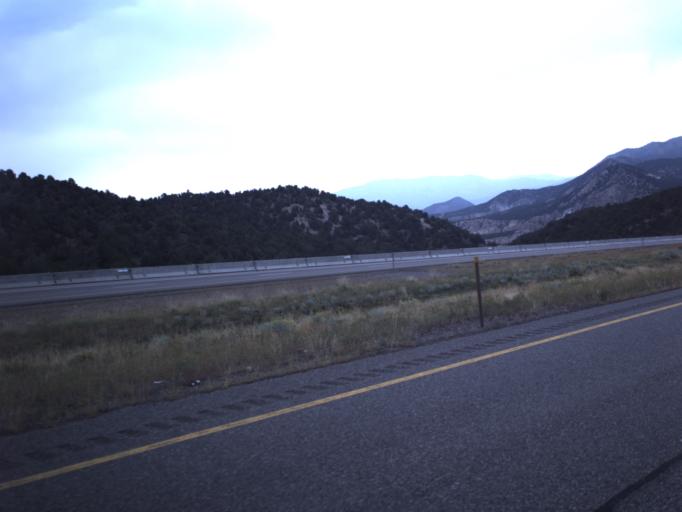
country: US
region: Utah
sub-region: Sevier County
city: Monroe
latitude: 38.5507
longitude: -112.3898
